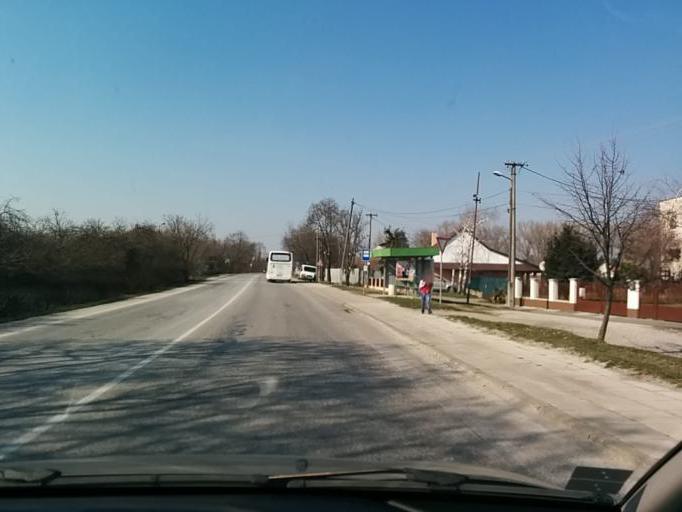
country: SK
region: Trnavsky
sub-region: Okres Galanta
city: Galanta
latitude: 48.2191
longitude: 17.7287
